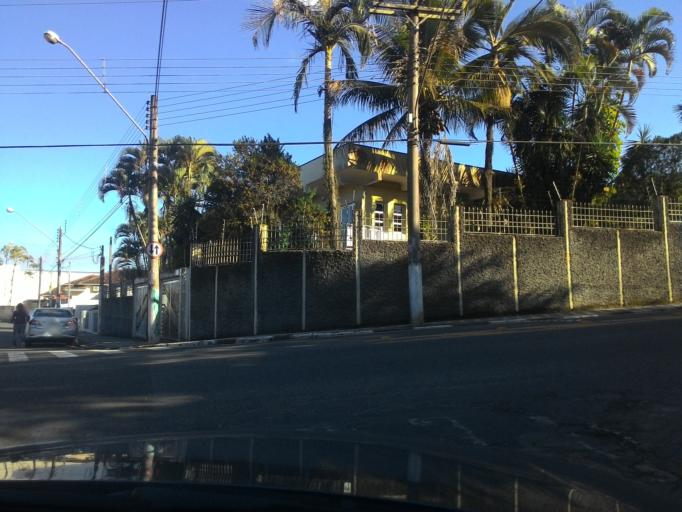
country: BR
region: Sao Paulo
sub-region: Registro
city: Registro
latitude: -24.4973
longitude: -47.8445
